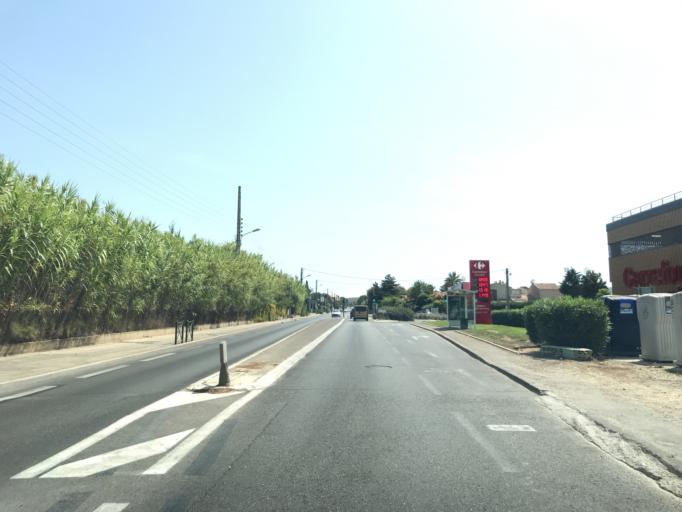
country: FR
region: Provence-Alpes-Cote d'Azur
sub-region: Departement du Var
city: Sanary-sur-Mer
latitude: 43.1040
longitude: 5.8187
